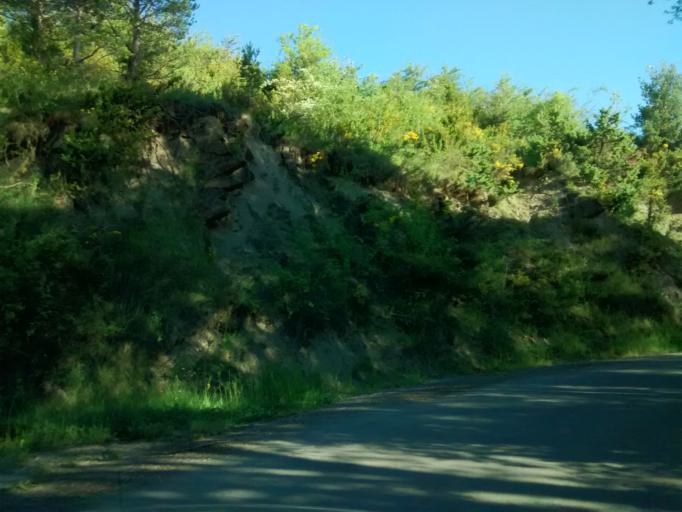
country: ES
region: Aragon
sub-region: Provincia de Huesca
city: Borau
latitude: 42.6839
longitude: -0.6209
